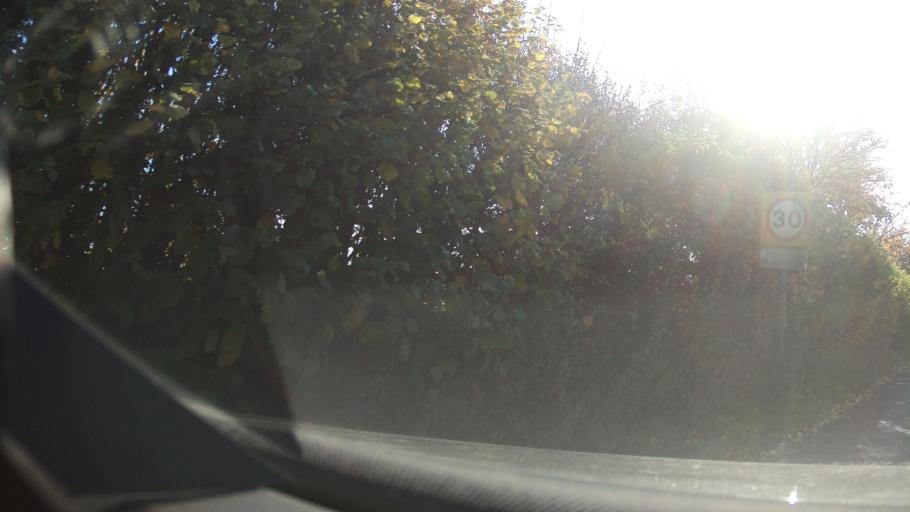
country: GB
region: England
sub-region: Somerset
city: Bruton
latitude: 51.0841
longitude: -2.4653
